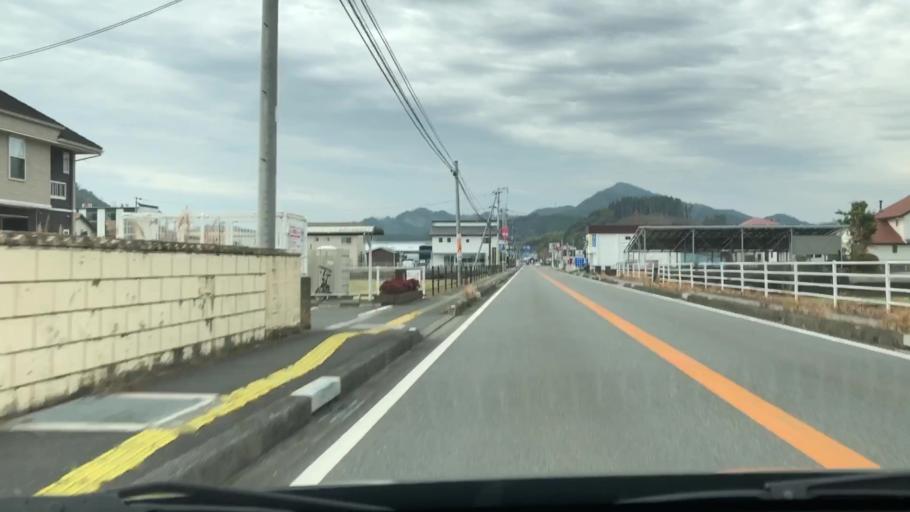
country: JP
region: Oita
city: Saiki
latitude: 32.9736
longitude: 131.8424
